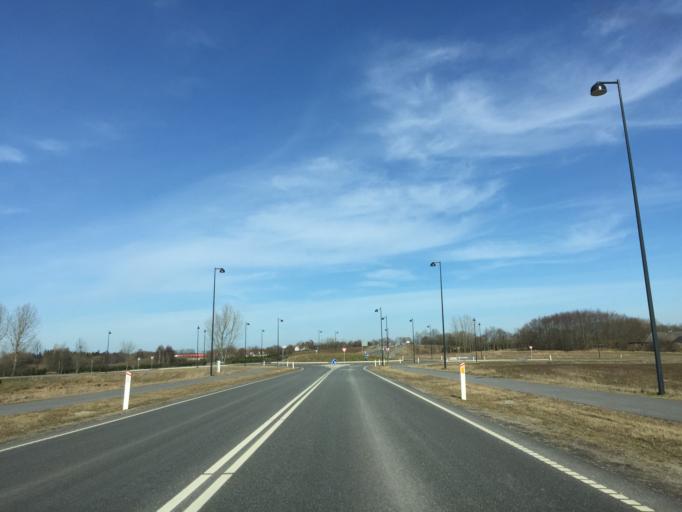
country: DK
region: Central Jutland
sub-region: Silkeborg Kommune
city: Silkeborg
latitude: 56.2032
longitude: 9.5537
